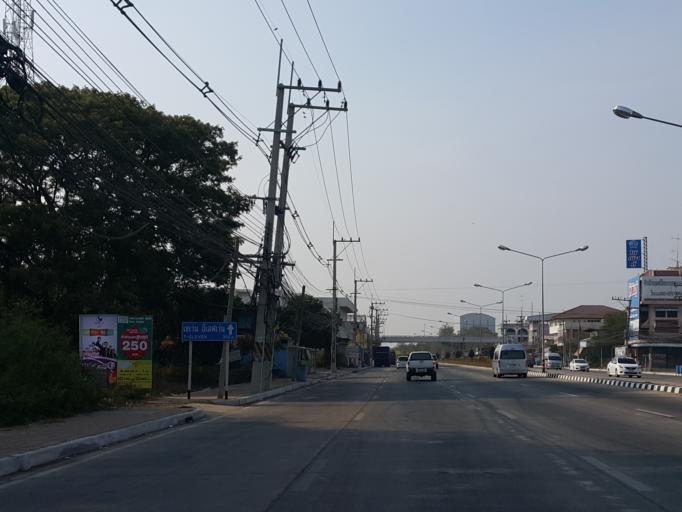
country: TH
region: Suphan Buri
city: Sam Chuk
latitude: 14.7529
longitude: 100.0972
